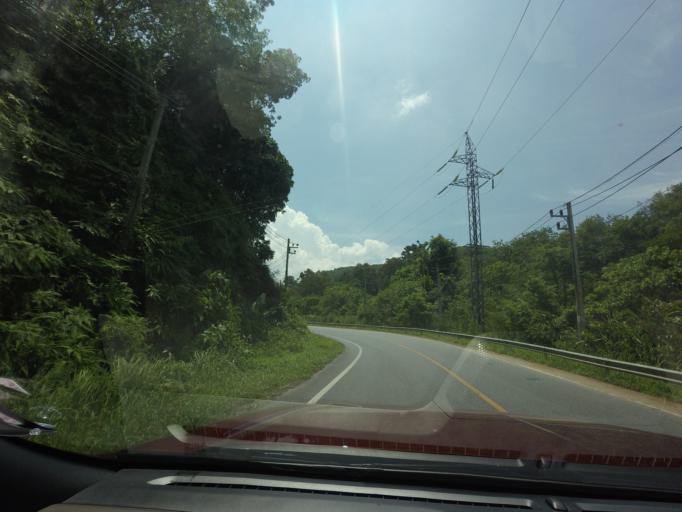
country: TH
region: Yala
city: Betong
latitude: 5.8859
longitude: 101.1456
